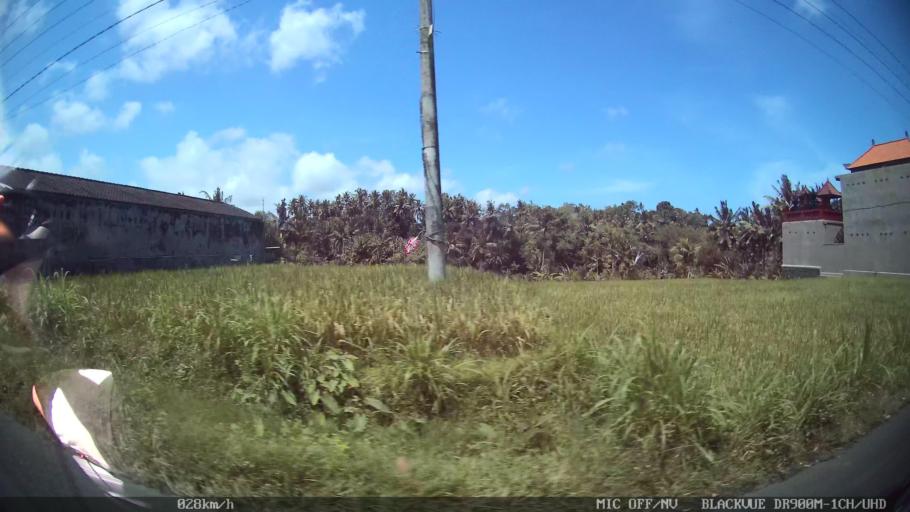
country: ID
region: Bali
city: Banjar Kelodan
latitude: -8.5324
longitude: 115.3355
